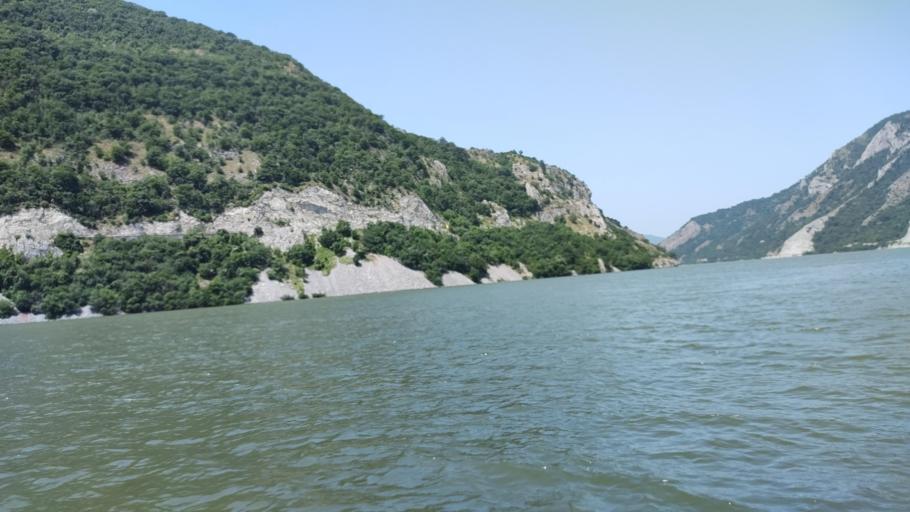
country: RO
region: Caras-Severin
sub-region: Comuna Berzasca
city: Berzasca
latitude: 44.5858
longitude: 22.0266
